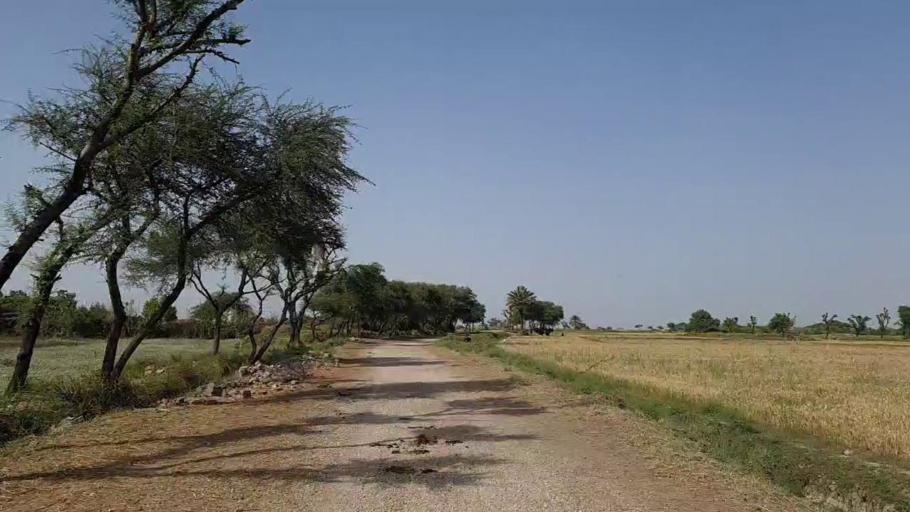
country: PK
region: Sindh
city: Jati
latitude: 24.3417
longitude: 68.3040
